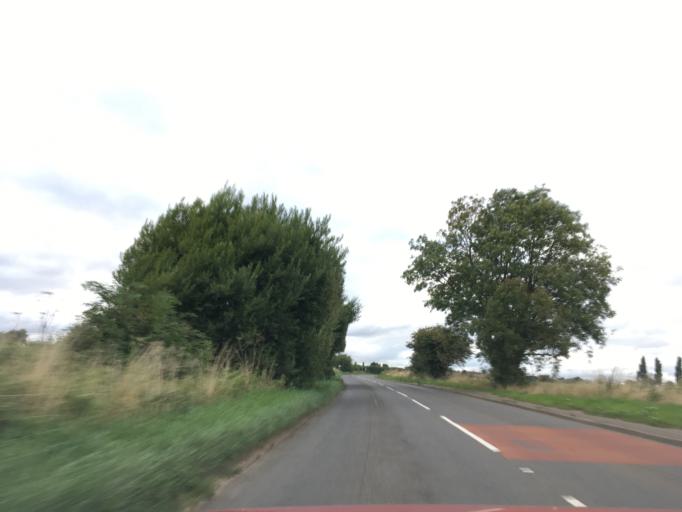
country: GB
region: England
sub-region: Wiltshire
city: Devizes
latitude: 51.3831
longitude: -2.0379
